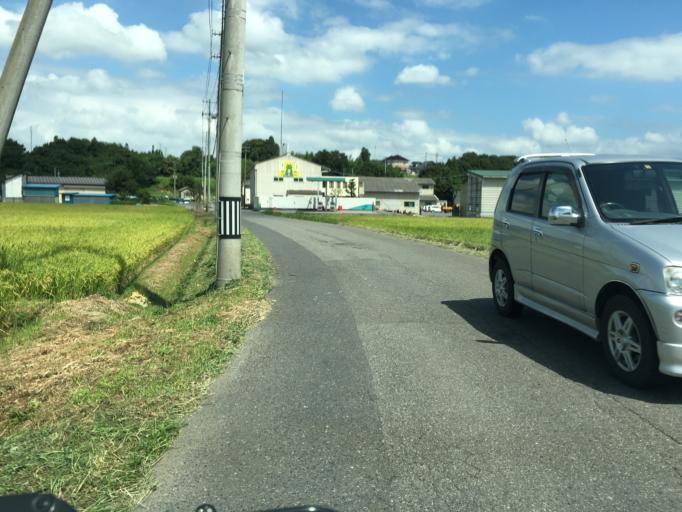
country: JP
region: Fukushima
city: Motomiya
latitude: 37.5180
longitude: 140.3846
